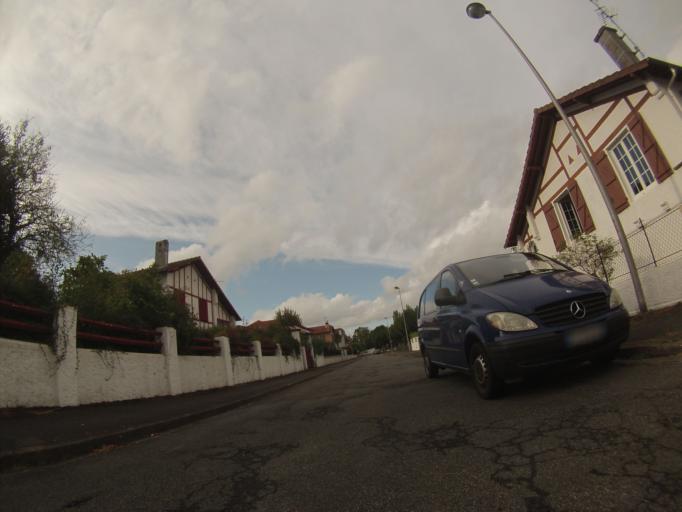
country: FR
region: Aquitaine
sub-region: Departement des Pyrenees-Atlantiques
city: Gelos
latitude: 43.2807
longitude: -0.3772
